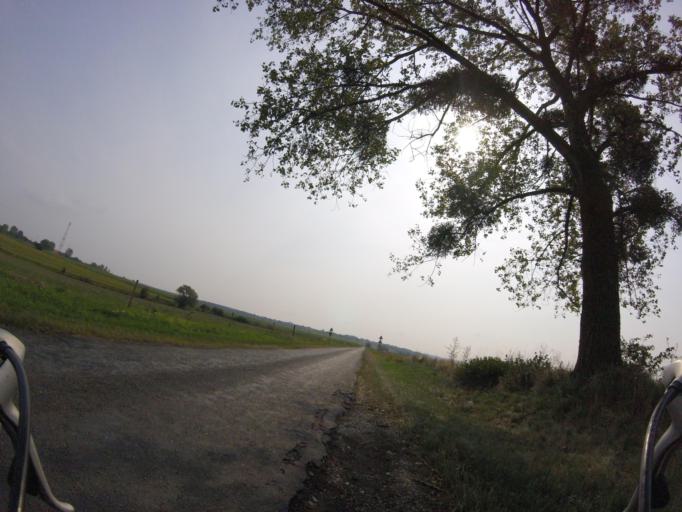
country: HU
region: Veszprem
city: Papa
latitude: 47.2438
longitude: 17.5213
